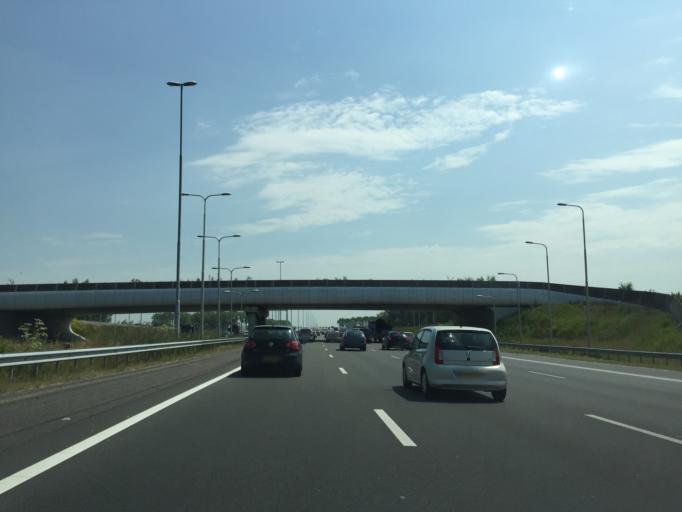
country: NL
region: Gelderland
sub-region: Gemeente Culemborg
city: Culemborg
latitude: 51.9178
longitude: 5.1751
